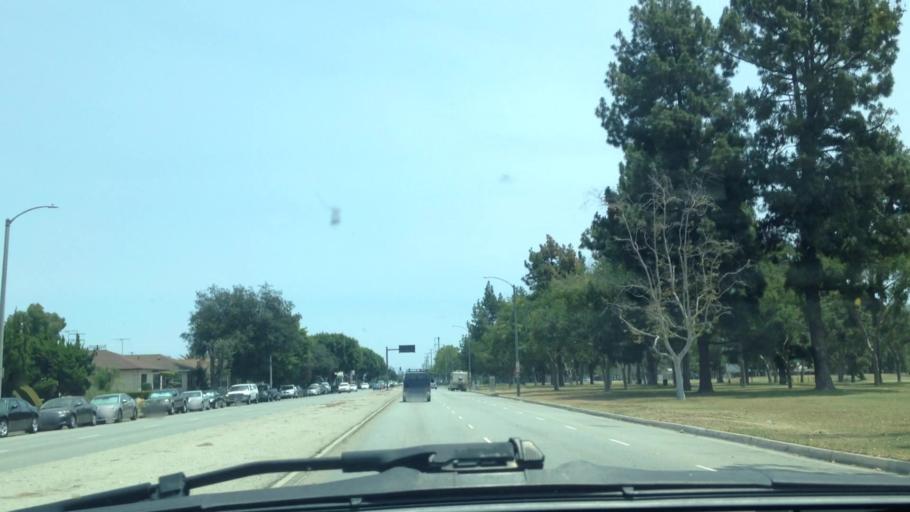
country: US
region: California
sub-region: Los Angeles County
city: Lakewood
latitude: 33.8323
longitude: -118.1296
